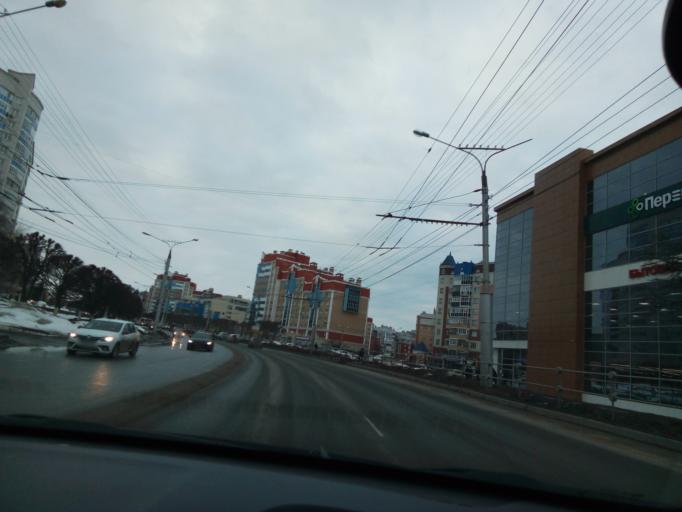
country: RU
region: Chuvashia
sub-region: Cheboksarskiy Rayon
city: Cheboksary
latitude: 56.1484
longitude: 47.2008
